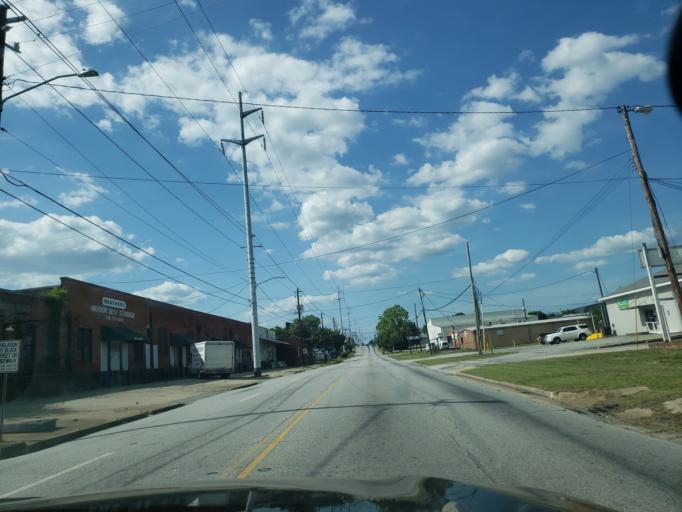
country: US
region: Georgia
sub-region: Muscogee County
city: Columbus
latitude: 32.4671
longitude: -84.9798
